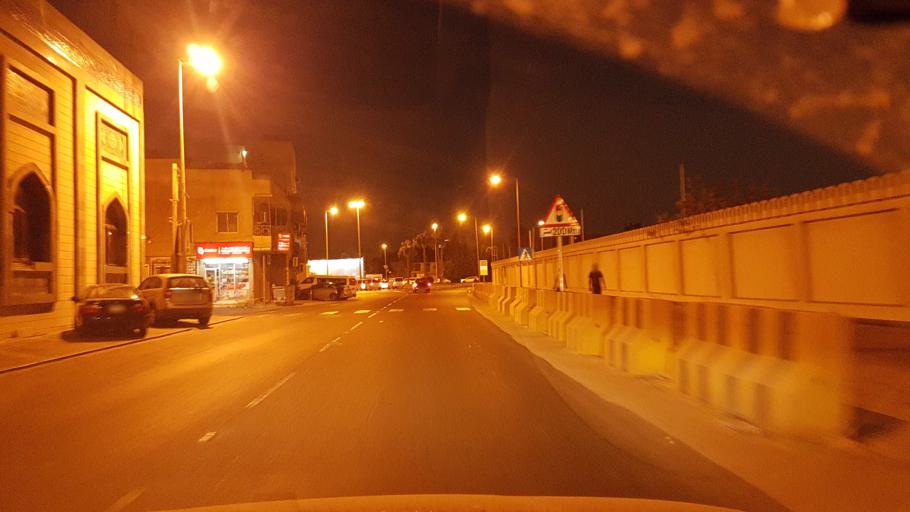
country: BH
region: Manama
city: Manama
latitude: 26.2208
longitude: 50.5782
